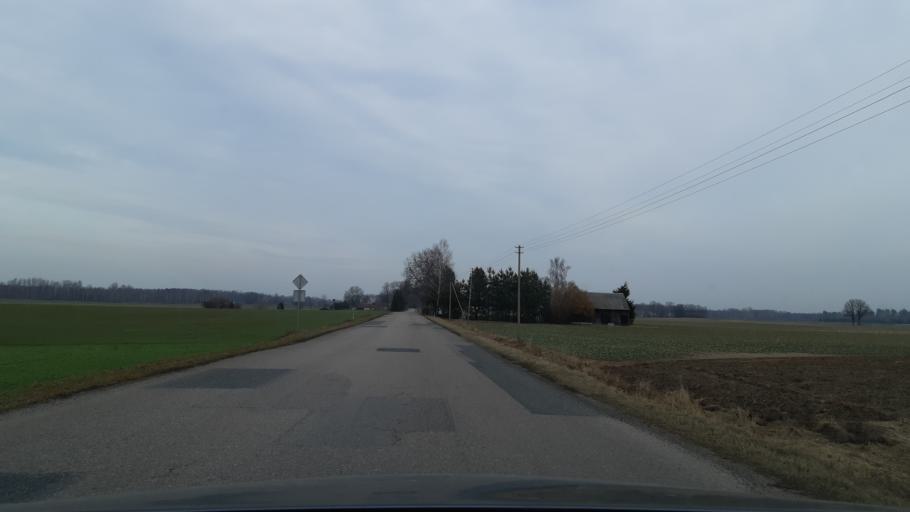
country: LT
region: Marijampoles apskritis
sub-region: Marijampole Municipality
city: Marijampole
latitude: 54.7176
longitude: 23.3323
